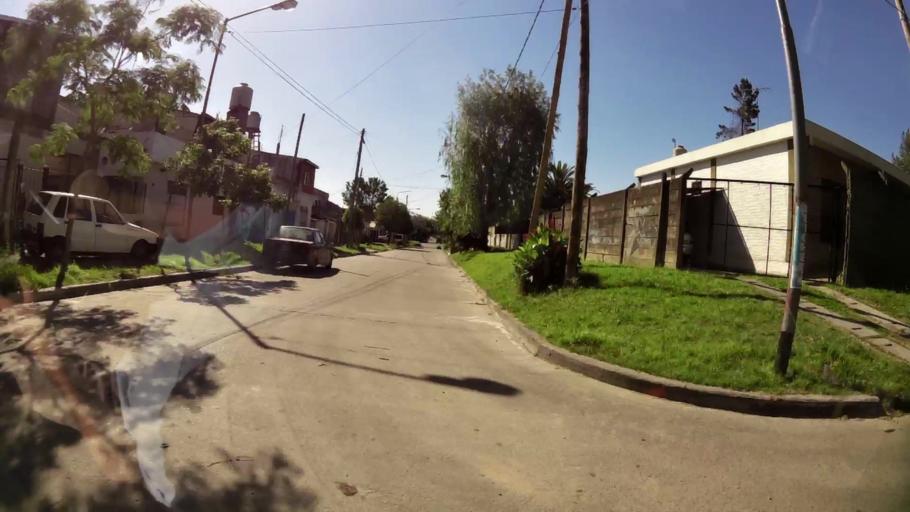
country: AR
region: Buenos Aires
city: Caseros
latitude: -34.5455
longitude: -58.5886
